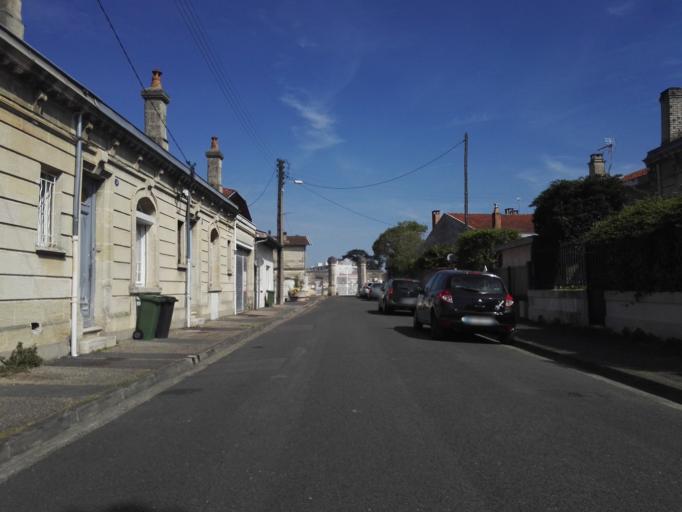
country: FR
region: Aquitaine
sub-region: Departement de la Gironde
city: Talence
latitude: 44.8147
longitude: -0.5848
